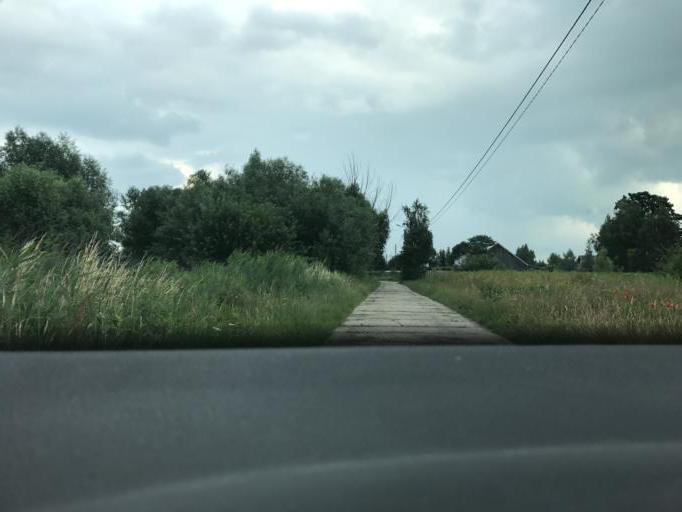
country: PL
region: Pomeranian Voivodeship
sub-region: Powiat gdanski
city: Cedry Wielkie
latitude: 54.3392
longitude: 18.8142
